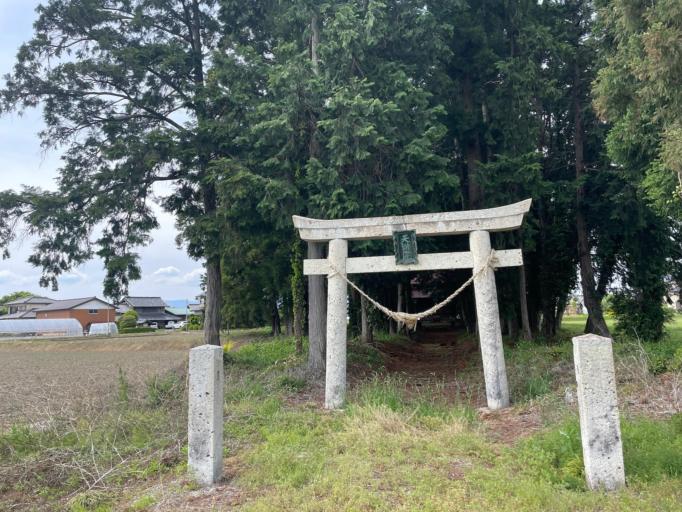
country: JP
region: Tochigi
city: Mibu
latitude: 36.4732
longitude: 139.7636
